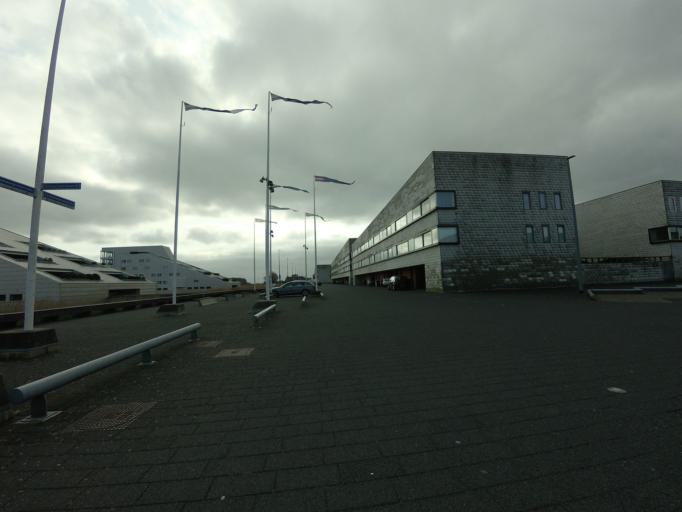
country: NL
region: North Holland
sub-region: Gemeente Huizen
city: Huizen
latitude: 52.2999
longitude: 5.2821
